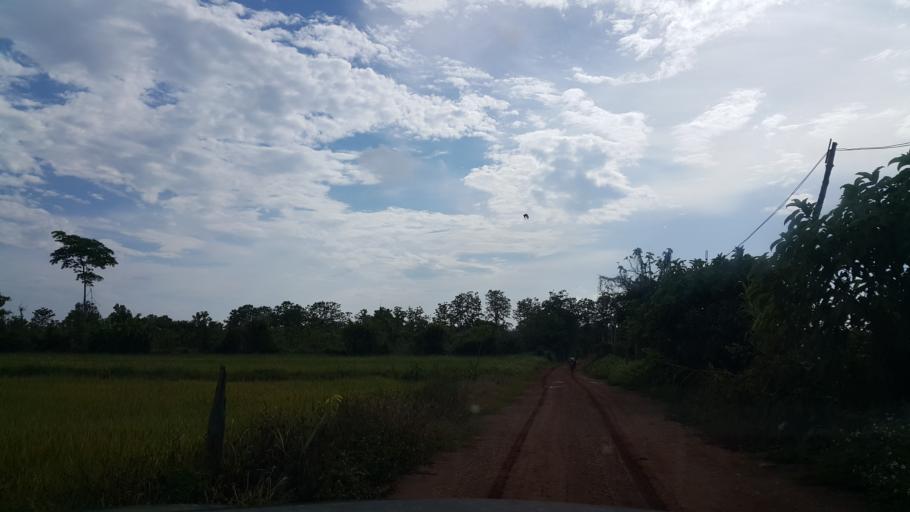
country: TH
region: Chiang Rai
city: Wiang Chai
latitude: 19.9751
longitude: 99.9088
